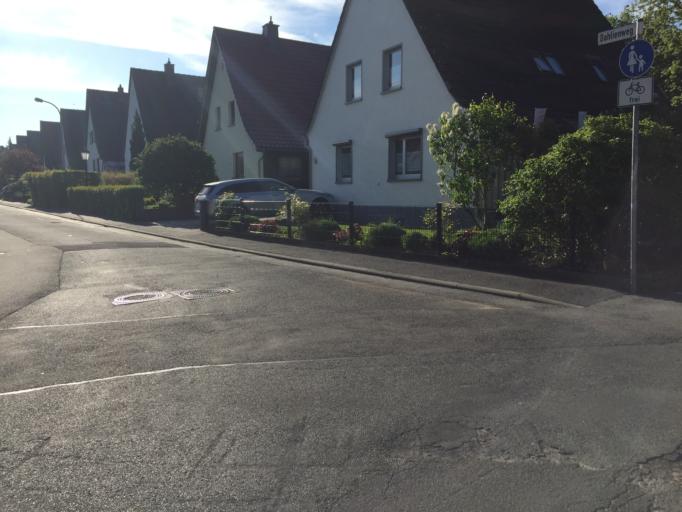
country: DE
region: Hesse
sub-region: Regierungsbezirk Giessen
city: Wetzlar
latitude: 50.5423
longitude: 8.5292
